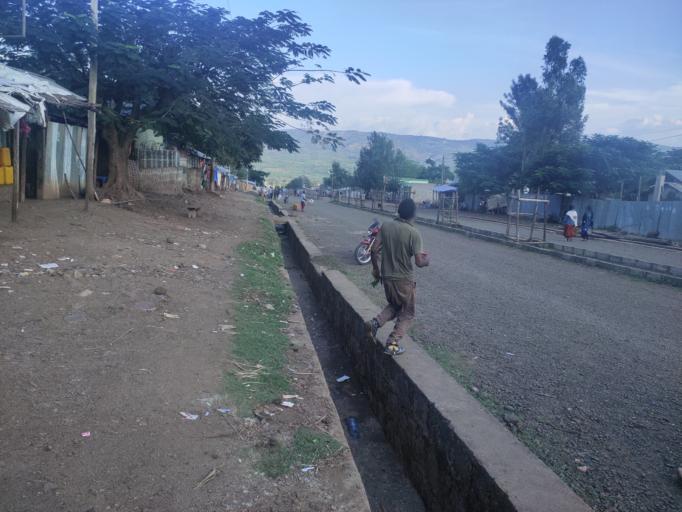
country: ET
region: Southern Nations, Nationalities, and People's Region
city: Felege Neway
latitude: 6.2509
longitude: 37.0166
